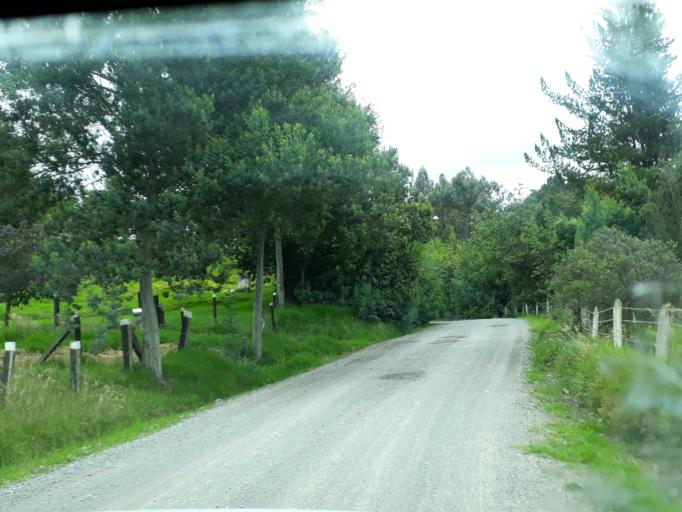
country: CO
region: Cundinamarca
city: La Mesa
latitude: 5.2907
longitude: -73.9051
